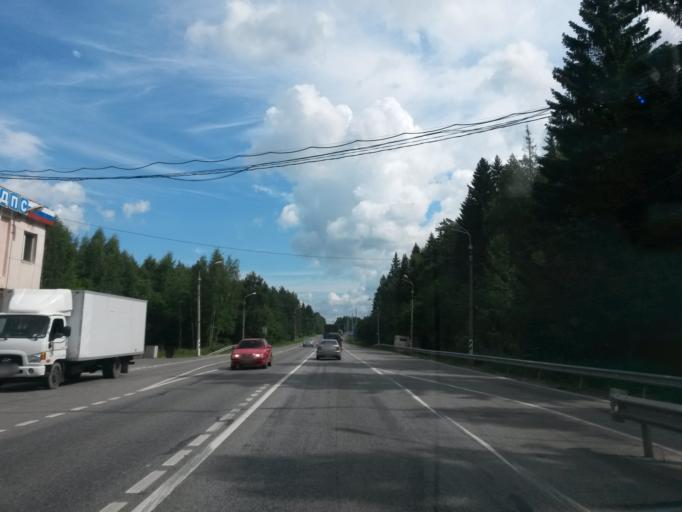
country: RU
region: Jaroslavl
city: Pereslavl'-Zalesskiy
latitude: 56.7012
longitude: 38.7831
